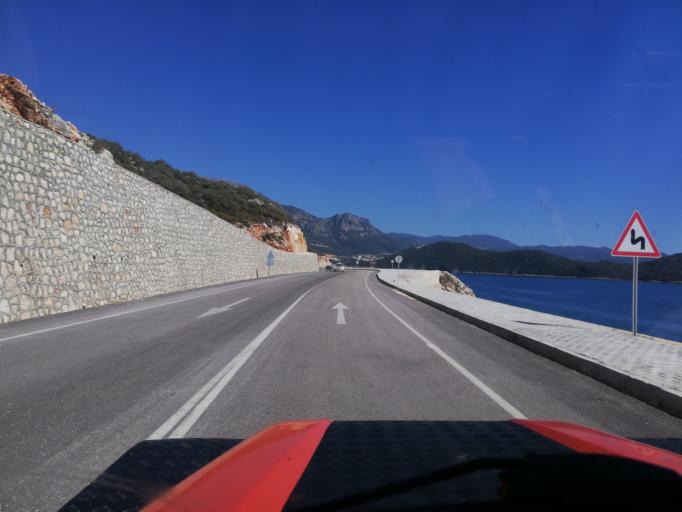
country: TR
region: Antalya
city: Kas
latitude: 36.2022
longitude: 29.5886
